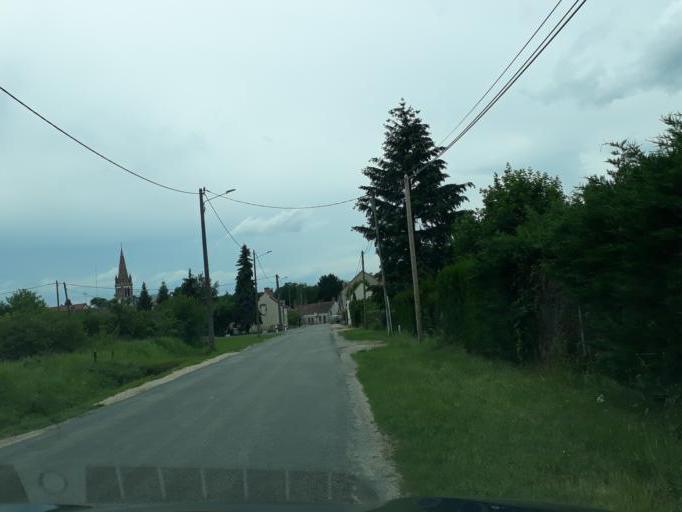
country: FR
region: Centre
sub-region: Departement du Loiret
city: Tigy
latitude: 47.7937
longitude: 2.2037
